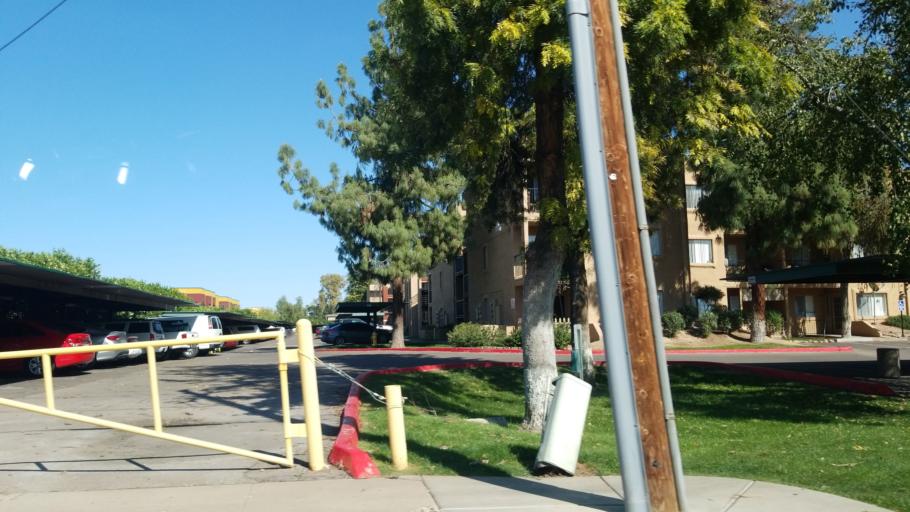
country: US
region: Arizona
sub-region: Maricopa County
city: Glendale
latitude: 33.5574
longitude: -112.1905
